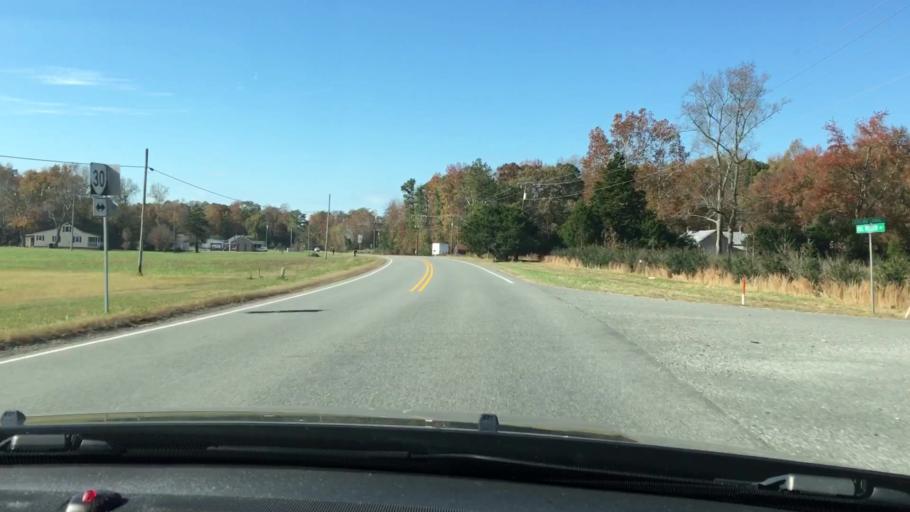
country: US
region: Virginia
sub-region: King William County
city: King William
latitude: 37.6722
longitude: -76.9742
